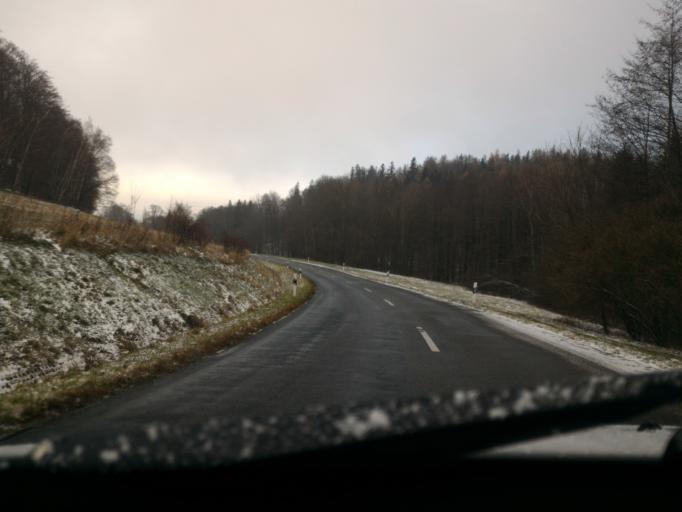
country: DE
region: Saxony
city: Grossschonau
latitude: 50.8608
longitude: 14.6584
